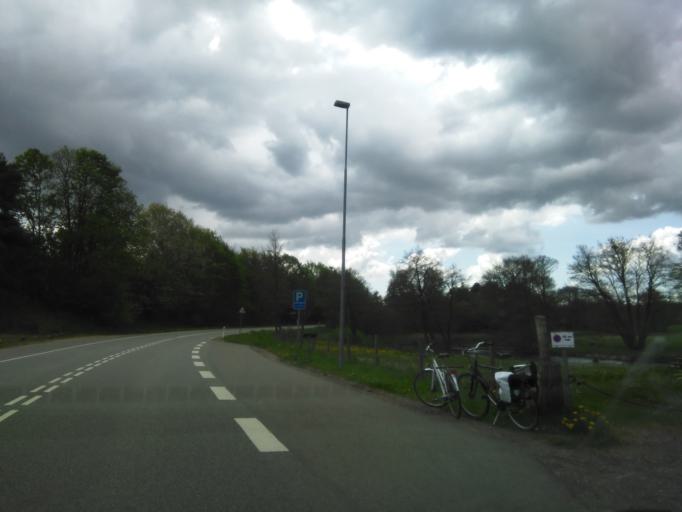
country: DK
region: Central Jutland
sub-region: Horsens Kommune
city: Braedstrup
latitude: 56.0129
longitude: 9.6984
